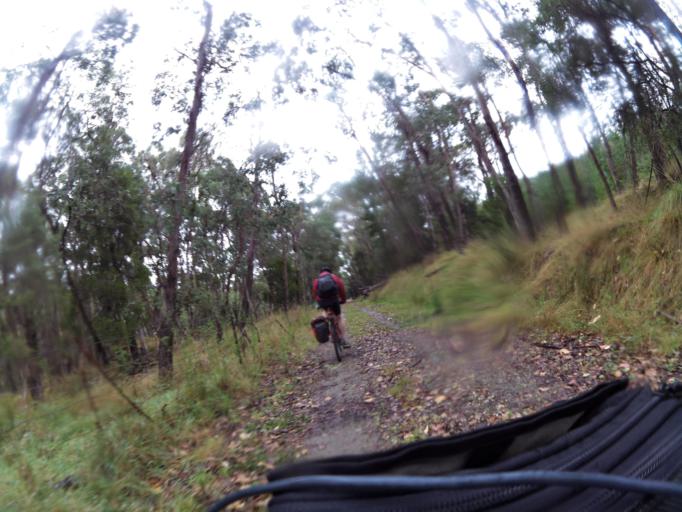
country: AU
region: New South Wales
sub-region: Greater Hume Shire
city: Holbrook
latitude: -36.1861
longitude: 147.5025
